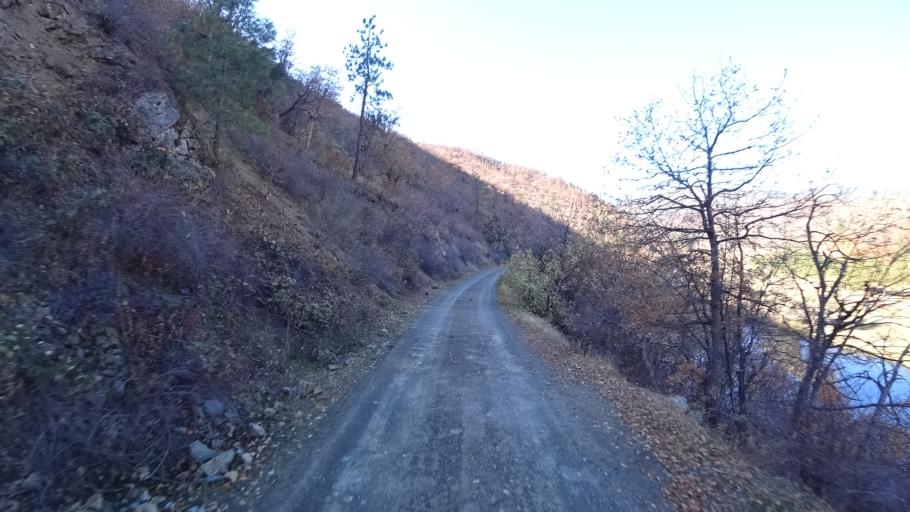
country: US
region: California
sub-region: Siskiyou County
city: Yreka
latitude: 41.8608
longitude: -122.7184
